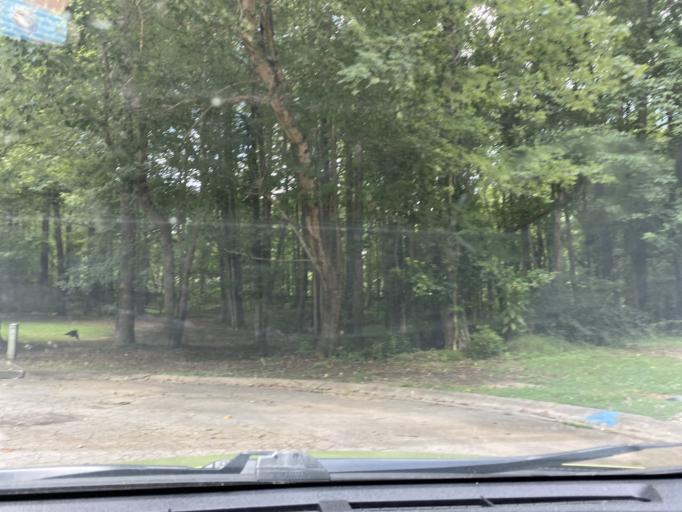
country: US
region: Georgia
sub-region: Fayette County
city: Peachtree City
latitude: 33.4176
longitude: -84.6927
